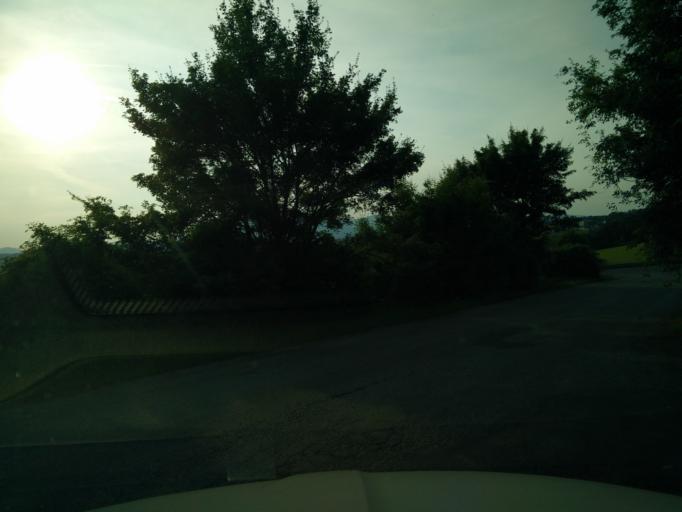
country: SK
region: Nitriansky
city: Prievidza
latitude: 48.7709
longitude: 18.6546
